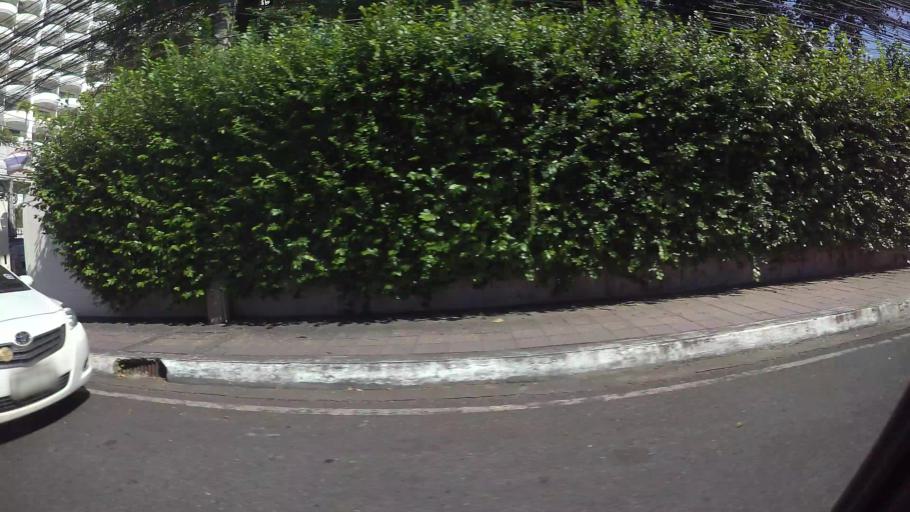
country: TH
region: Chon Buri
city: Phatthaya
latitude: 12.9153
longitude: 100.8648
